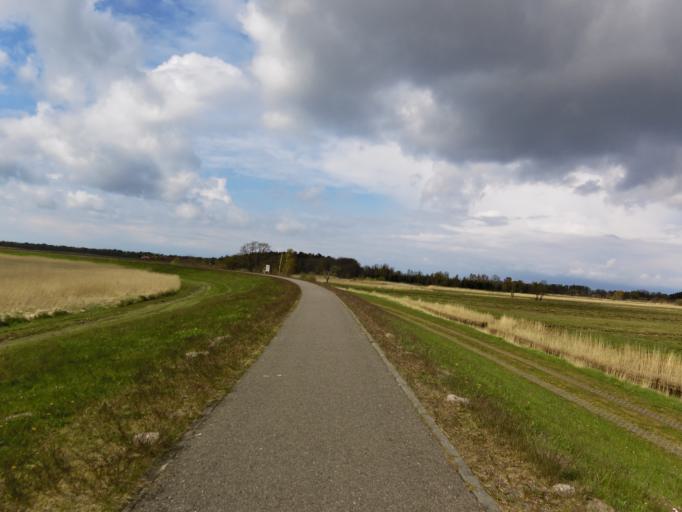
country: DE
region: Mecklenburg-Vorpommern
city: Zingst
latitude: 54.4322
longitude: 12.7261
